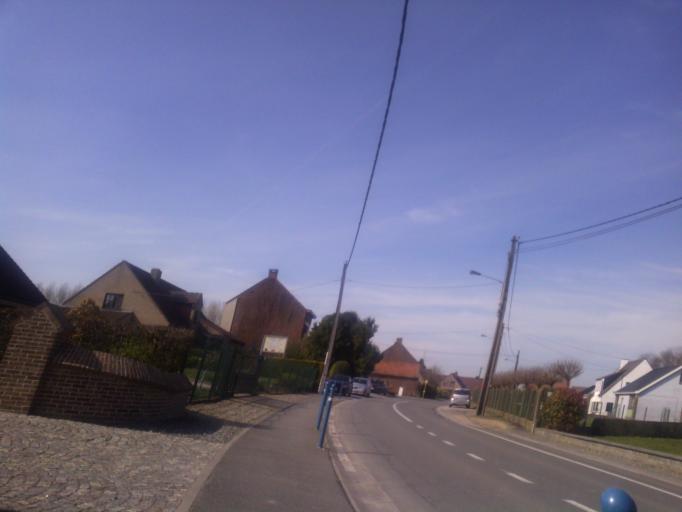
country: BE
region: Wallonia
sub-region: Province du Hainaut
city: Silly
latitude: 50.6505
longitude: 3.9208
